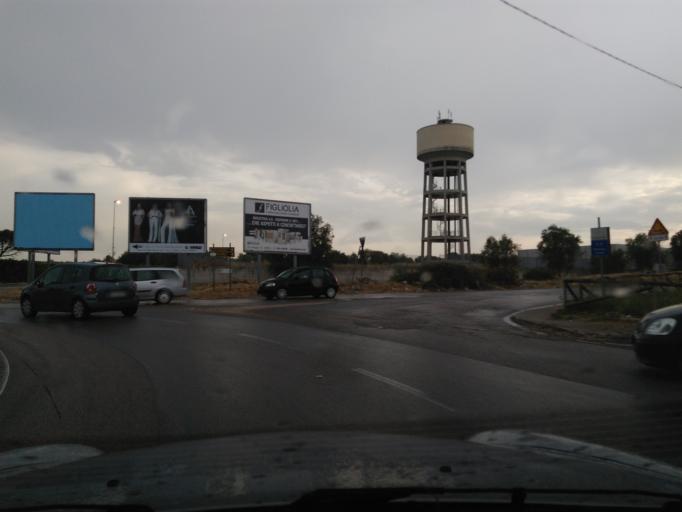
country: IT
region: Apulia
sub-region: Provincia di Bari
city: Molfetta
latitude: 41.2047
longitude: 16.5587
